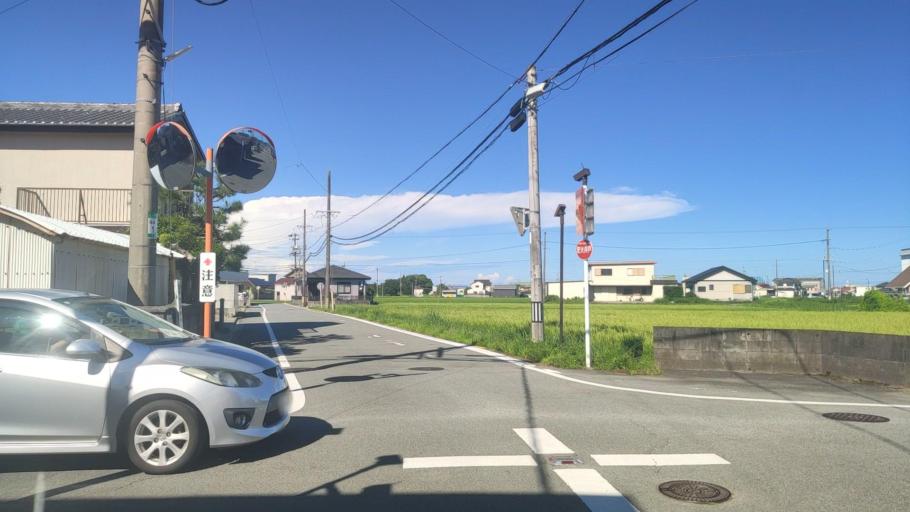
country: JP
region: Mie
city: Ise
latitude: 34.5114
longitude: 136.7161
